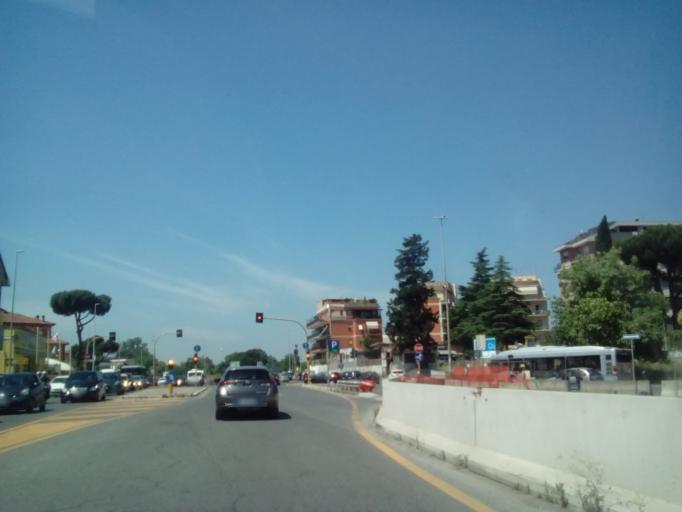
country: IT
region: Latium
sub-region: Citta metropolitana di Roma Capitale
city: Rome
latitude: 41.9248
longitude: 12.5723
